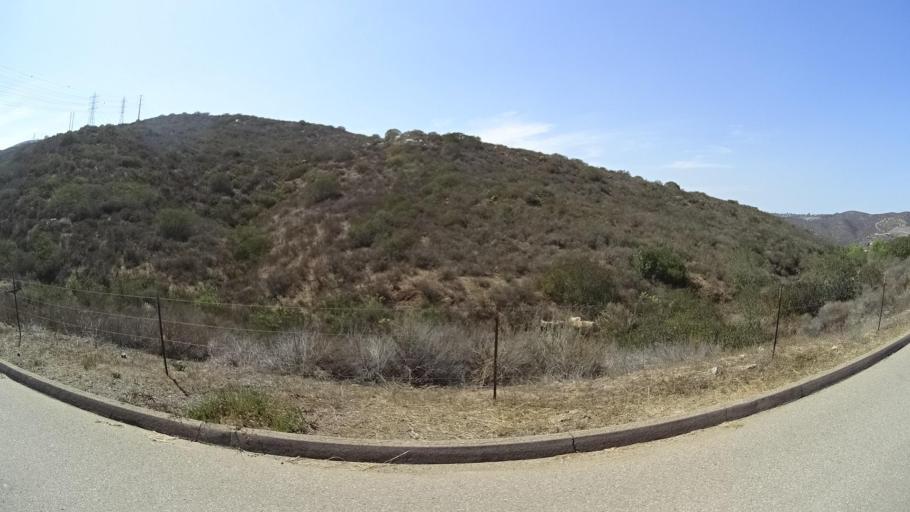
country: US
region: California
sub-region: San Diego County
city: Rancho San Diego
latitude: 32.7235
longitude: -116.9317
